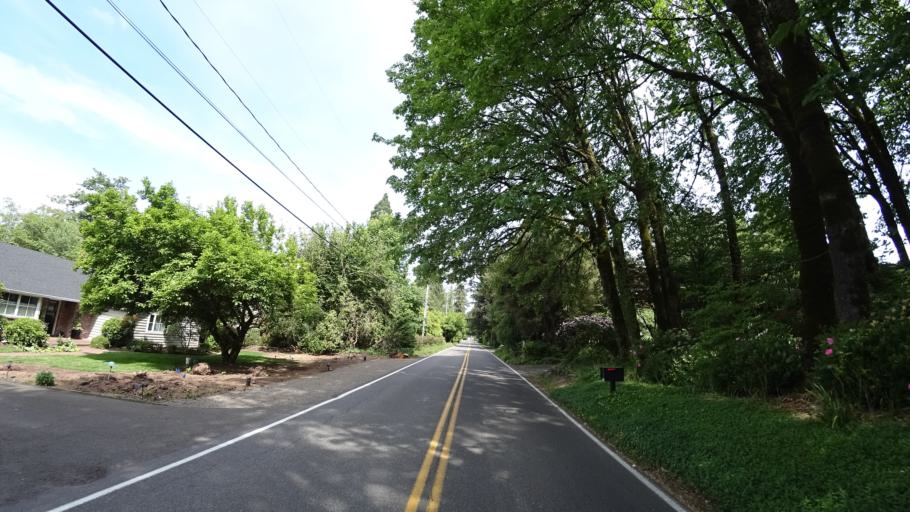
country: US
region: Oregon
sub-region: Clackamas County
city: Lake Oswego
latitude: 45.4412
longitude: -122.6667
